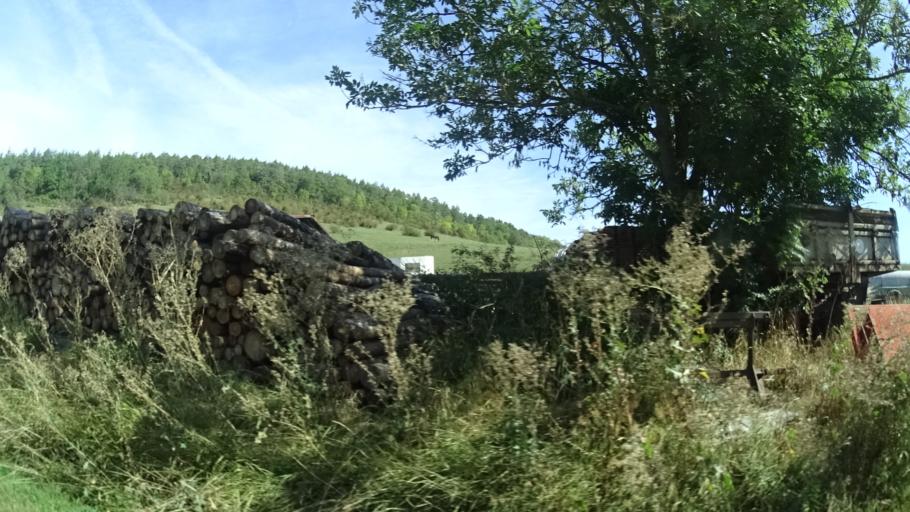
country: DE
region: Thuringia
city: Rottenbach
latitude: 50.7518
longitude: 11.1793
